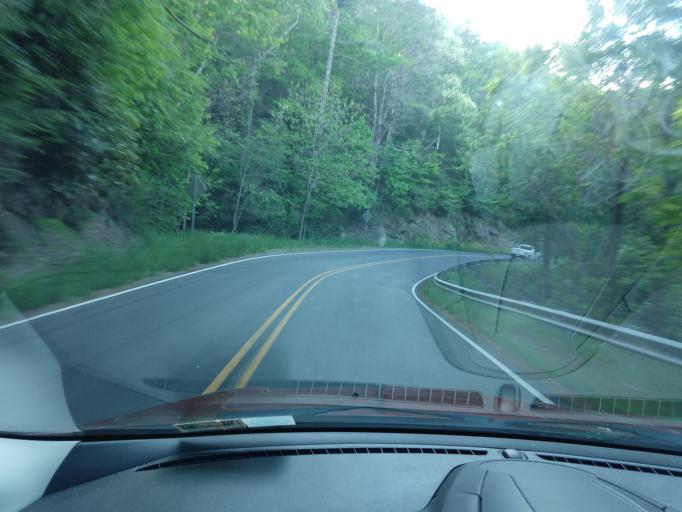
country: US
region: Virginia
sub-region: City of Galax
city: Galax
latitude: 36.7209
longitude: -80.9836
